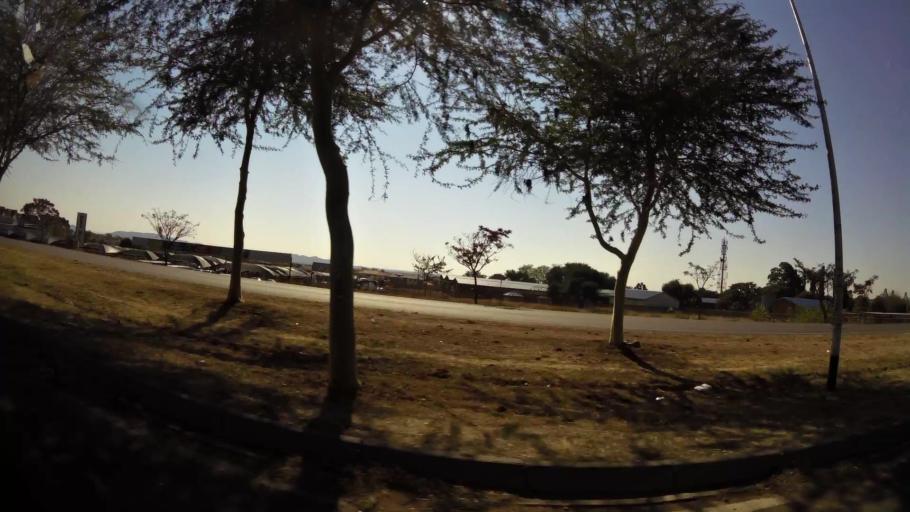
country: ZA
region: Gauteng
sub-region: City of Tshwane Metropolitan Municipality
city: Pretoria
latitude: -25.6816
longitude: 28.2665
